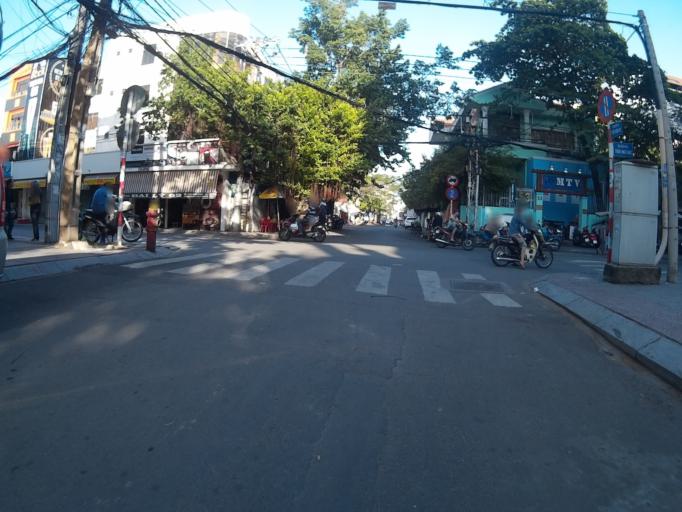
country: VN
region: Ho Chi Minh City
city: Quan Binh Thanh
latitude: 10.7941
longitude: 106.6892
